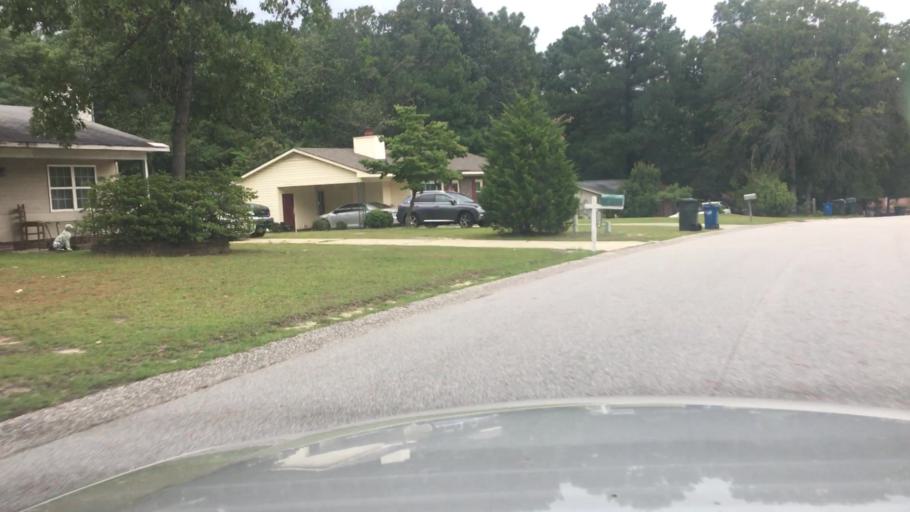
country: US
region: North Carolina
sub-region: Hoke County
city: Rockfish
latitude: 35.0112
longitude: -79.0208
